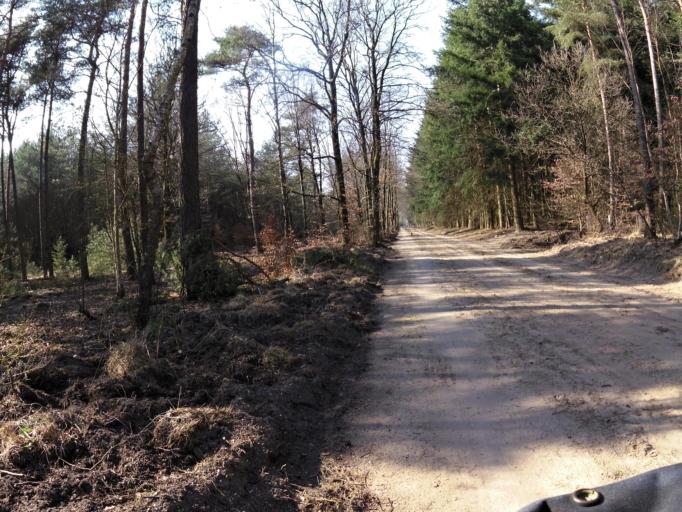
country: NL
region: Gelderland
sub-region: Gemeente Epe
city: Epe
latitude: 52.3664
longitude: 5.9472
